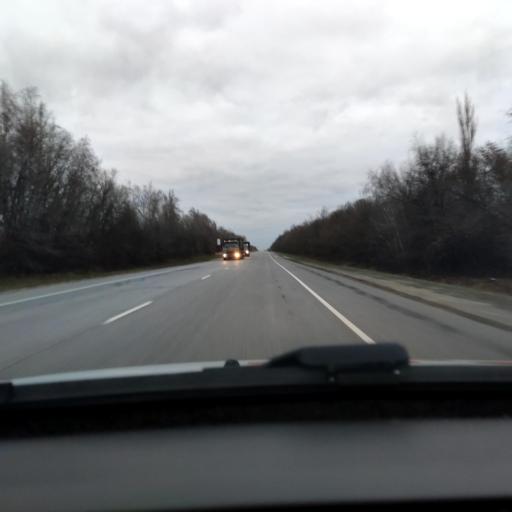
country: RU
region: Lipetsk
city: Khlevnoye
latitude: 52.3418
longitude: 39.1852
